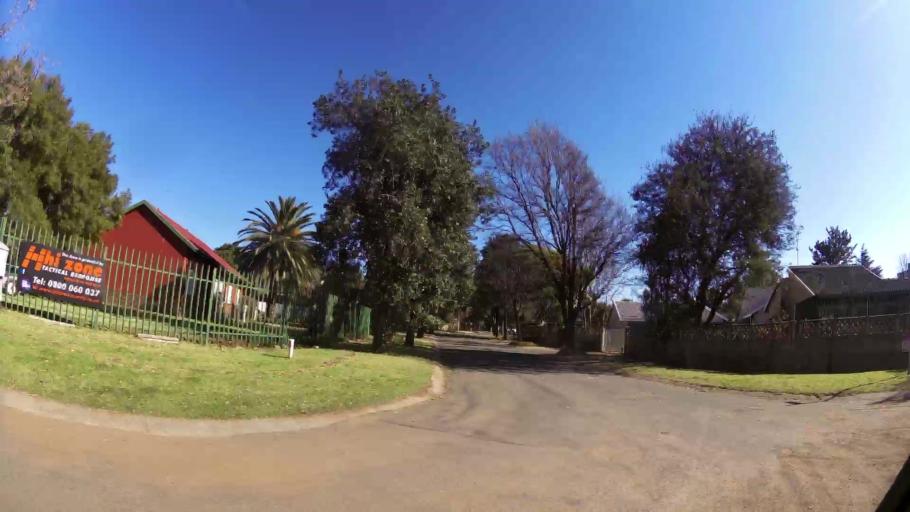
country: ZA
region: Gauteng
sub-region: Ekurhuleni Metropolitan Municipality
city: Germiston
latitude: -26.3301
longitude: 28.1056
